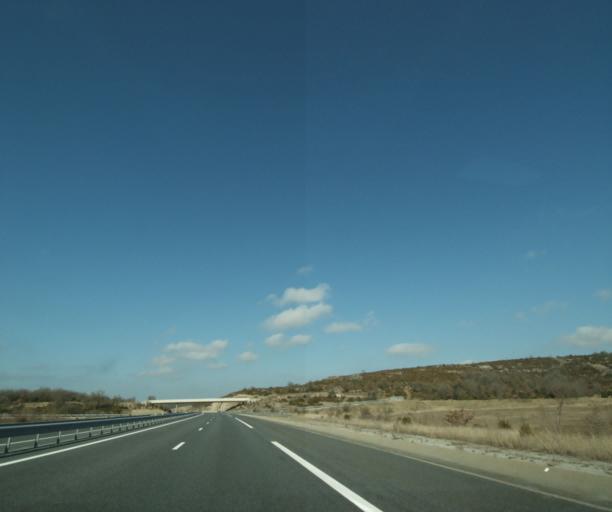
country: FR
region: Midi-Pyrenees
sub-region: Departement de l'Aveyron
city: Creissels
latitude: 44.0510
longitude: 3.0488
